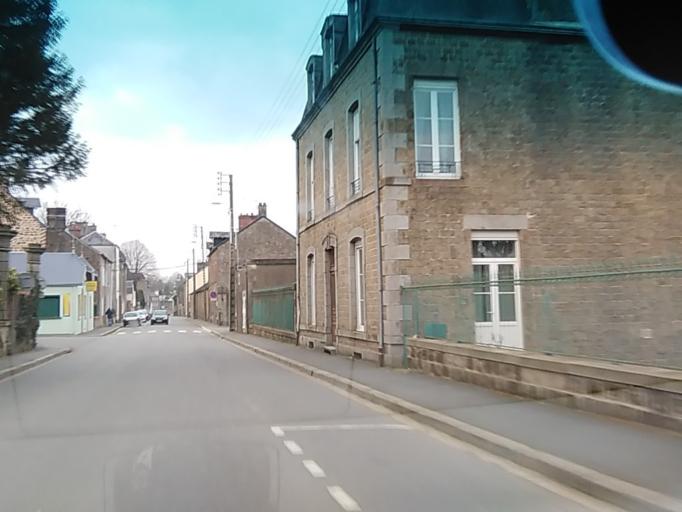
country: FR
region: Lower Normandy
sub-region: Departement de l'Orne
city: La Ferte-Mace
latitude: 48.5917
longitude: -0.3541
